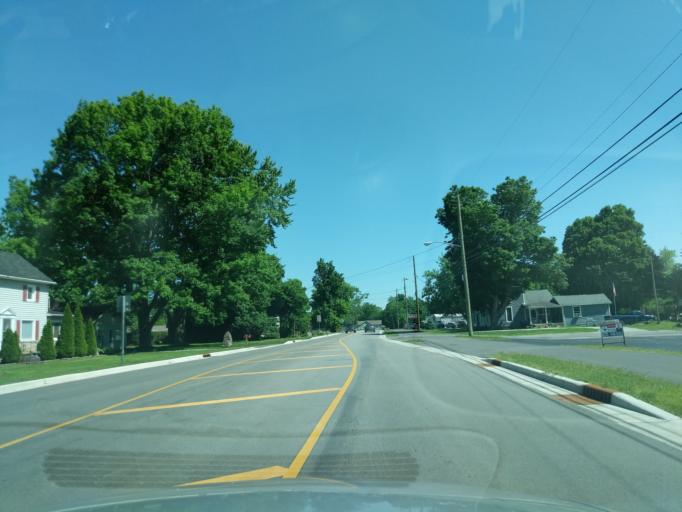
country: US
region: Indiana
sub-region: Huntington County
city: Huntington
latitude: 40.8600
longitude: -85.5069
